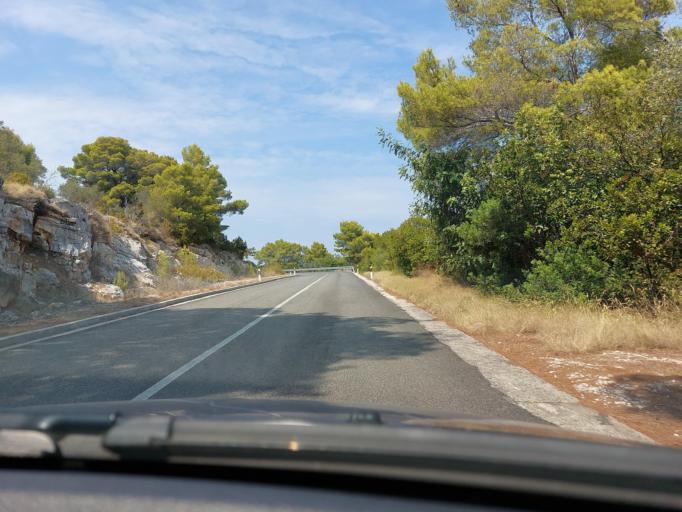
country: HR
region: Dubrovacko-Neretvanska
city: Smokvica
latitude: 42.7673
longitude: 16.8720
